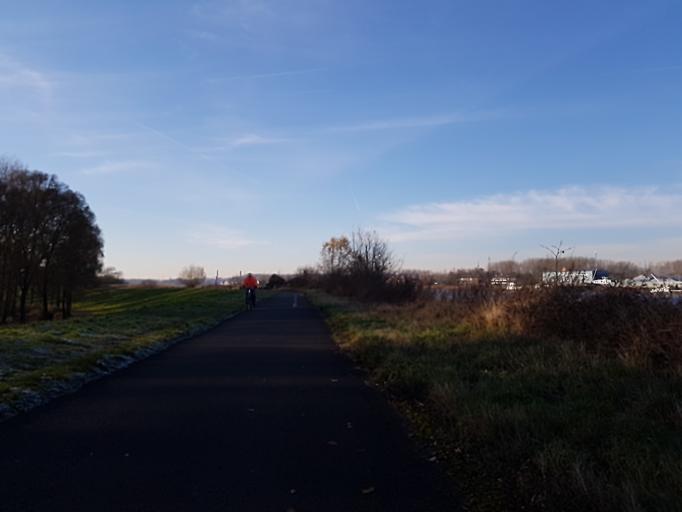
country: BE
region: Flanders
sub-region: Provincie Antwerpen
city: Niel
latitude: 51.1221
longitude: 4.2895
